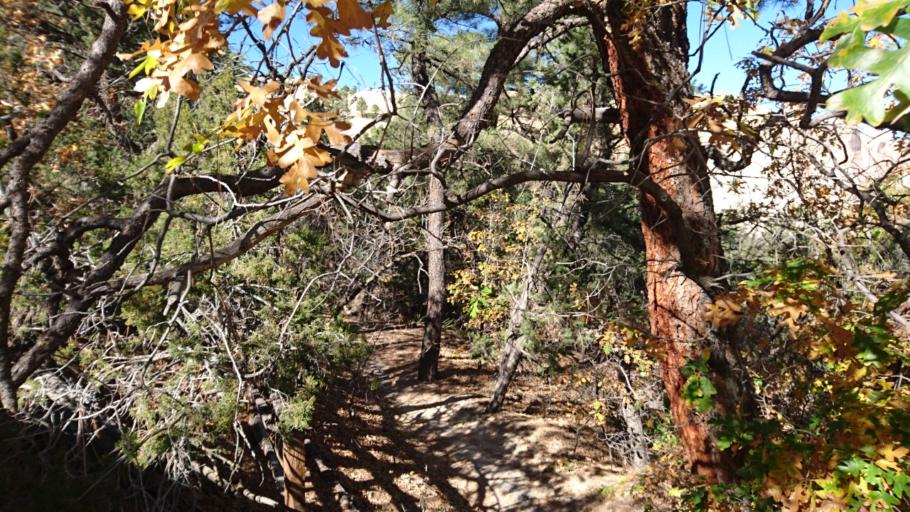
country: US
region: New Mexico
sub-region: McKinley County
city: Thoreau
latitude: 35.0376
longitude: -108.3523
